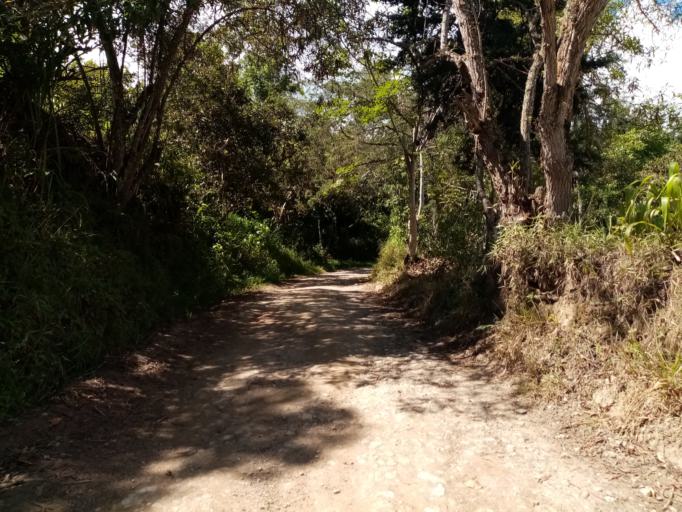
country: CO
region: Cundinamarca
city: Tenza
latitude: 5.0780
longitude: -73.4290
